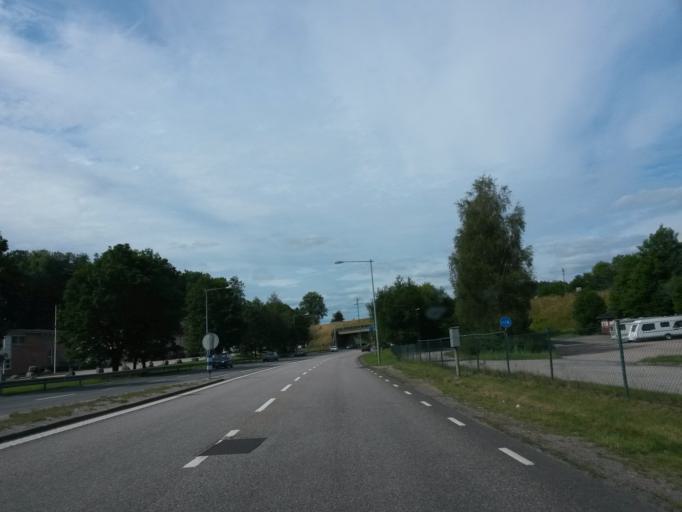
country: SE
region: Vaestra Goetaland
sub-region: Boras Kommun
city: Boras
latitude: 57.7050
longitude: 12.9501
